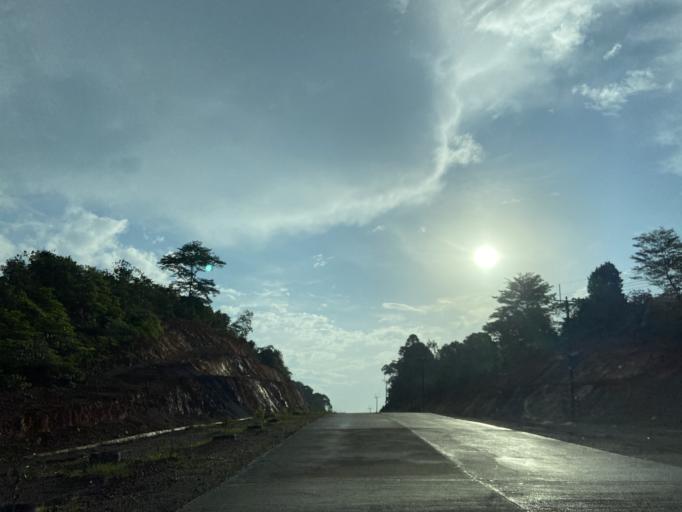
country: ID
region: Riau Islands
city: Tanjungpinang
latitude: 0.8971
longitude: 104.1270
